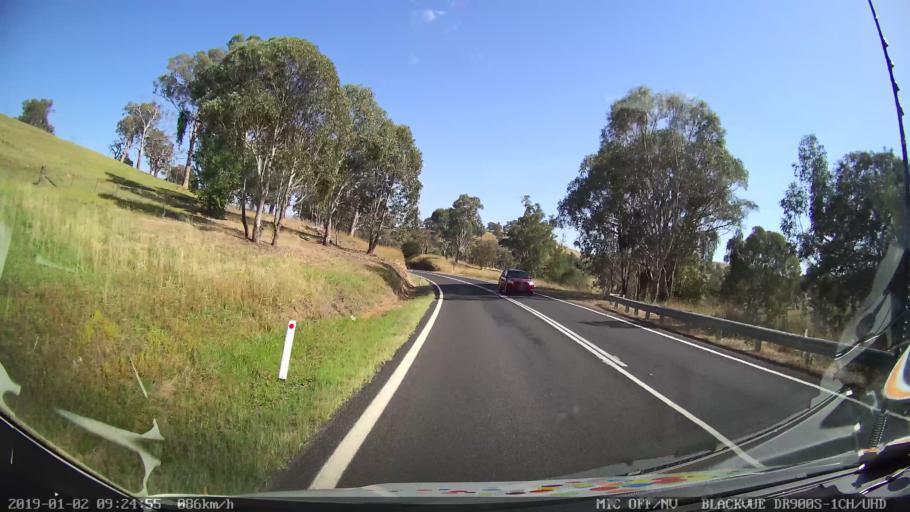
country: AU
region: New South Wales
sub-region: Tumut Shire
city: Tumut
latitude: -35.3707
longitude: 148.2920
